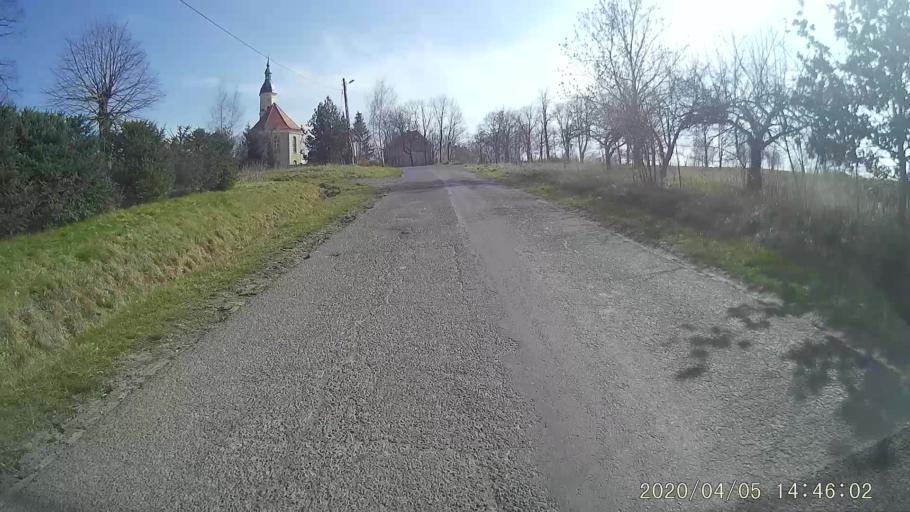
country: PL
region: Lower Silesian Voivodeship
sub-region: Powiat zgorzelecki
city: Sulikow
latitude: 51.0551
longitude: 15.1083
